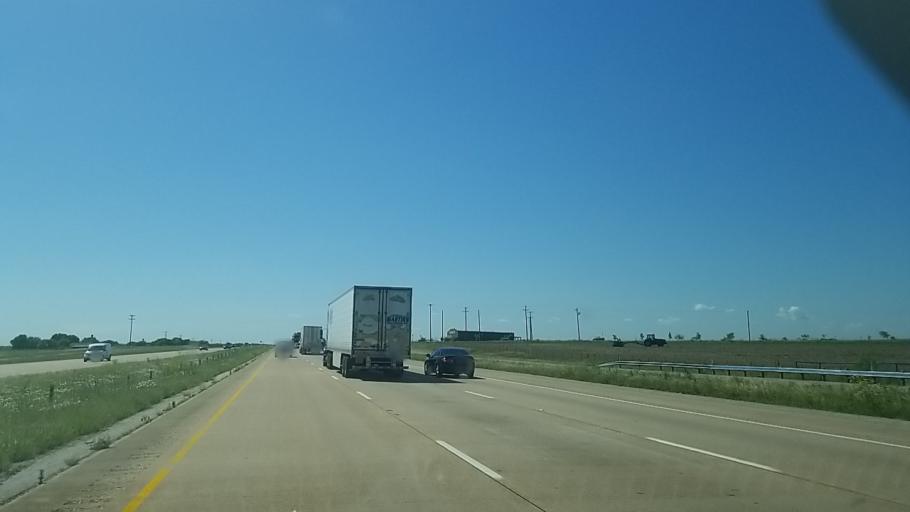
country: US
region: Texas
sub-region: Ellis County
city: Ennis
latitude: 32.2765
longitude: -96.5232
